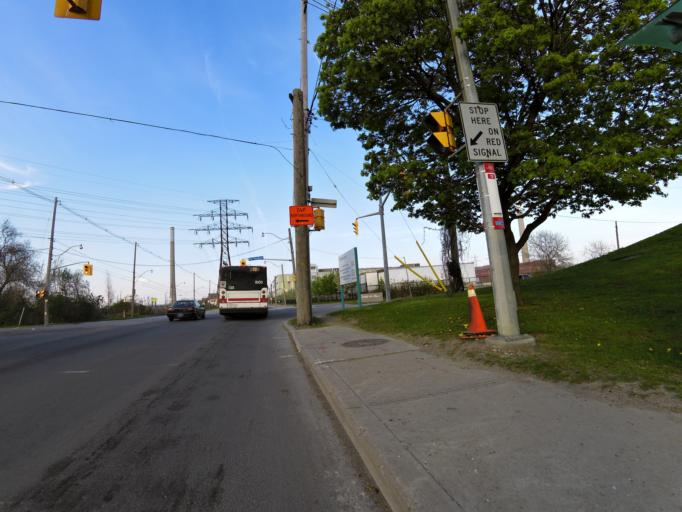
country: CA
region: Ontario
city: Toronto
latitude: 43.6484
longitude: -79.3452
